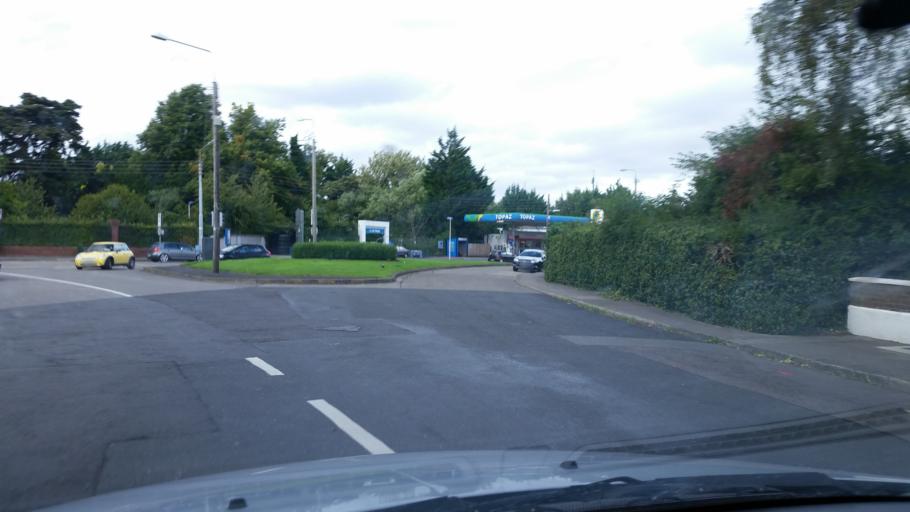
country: IE
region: Leinster
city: Templeogue
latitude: 53.3097
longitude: -6.3027
